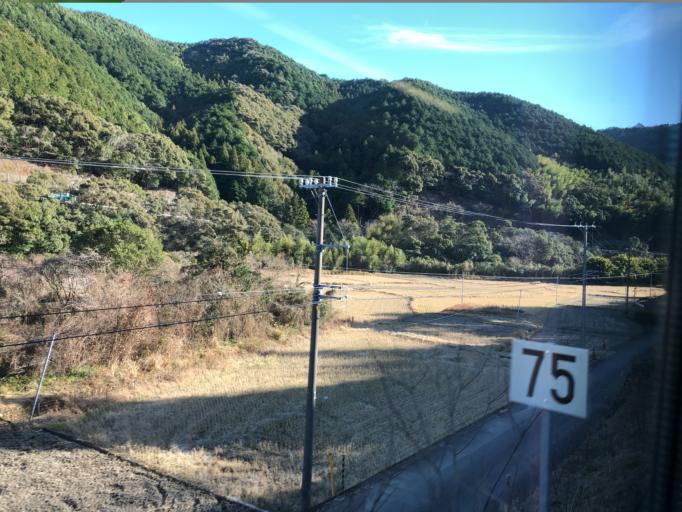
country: JP
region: Kochi
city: Nakamura
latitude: 33.1141
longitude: 133.1116
